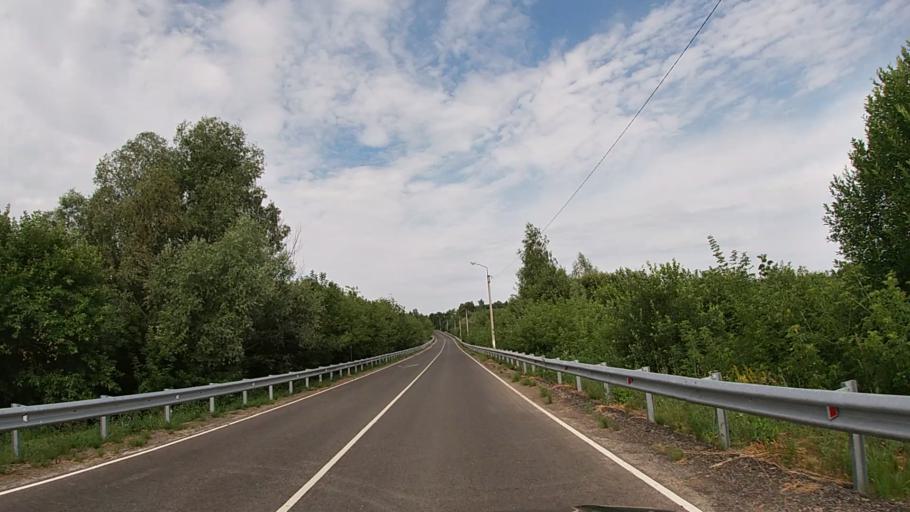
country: UA
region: Sumy
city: Krasnopillya
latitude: 50.8139
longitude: 35.4280
